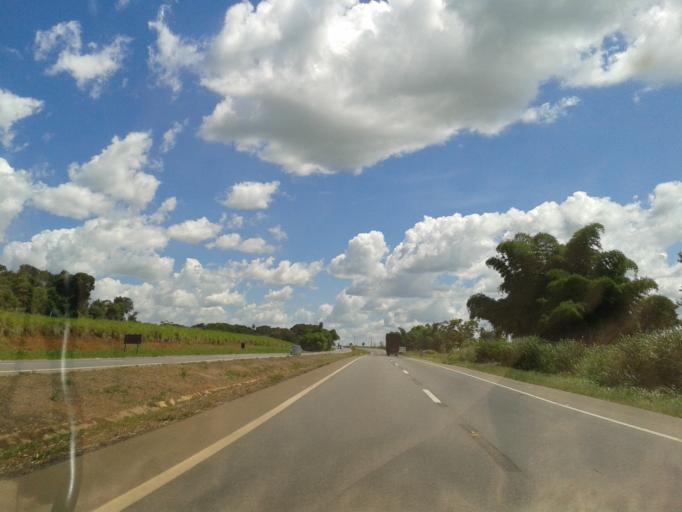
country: BR
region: Goias
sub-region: Piracanjuba
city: Piracanjuba
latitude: -17.2674
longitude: -49.2408
